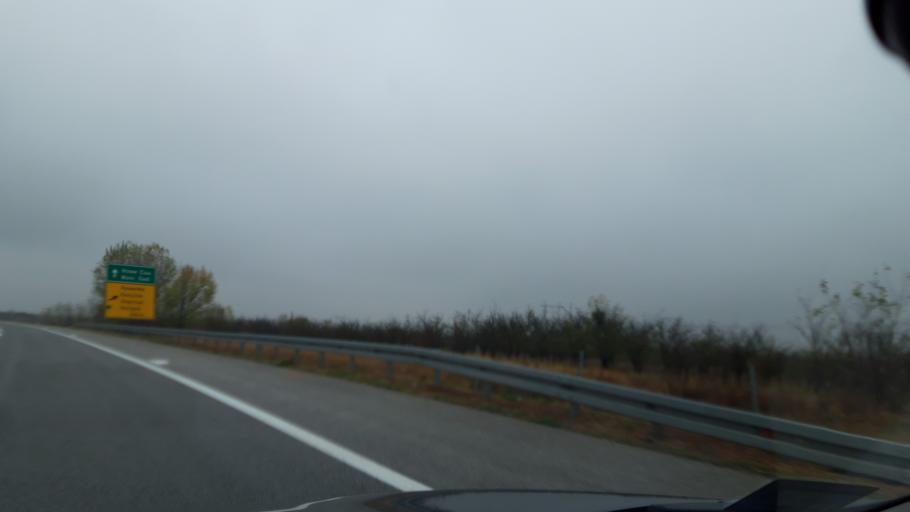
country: HU
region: Csongrad
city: Morahalom
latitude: 46.1601
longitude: 19.9432
